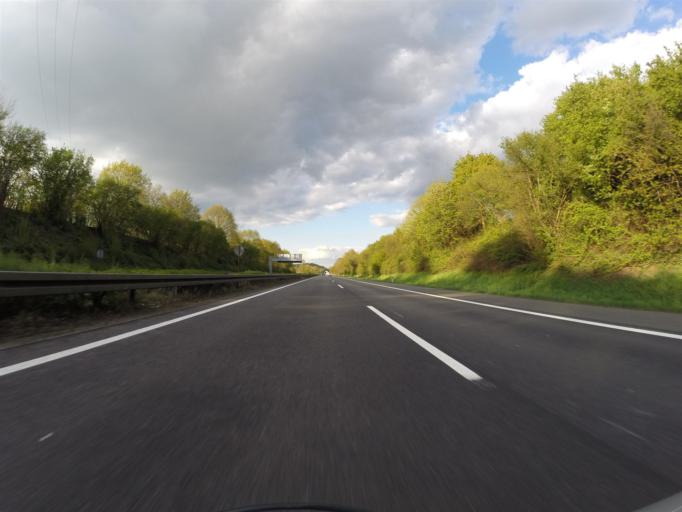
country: DE
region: Saarland
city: Bexbach
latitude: 49.3175
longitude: 7.2634
